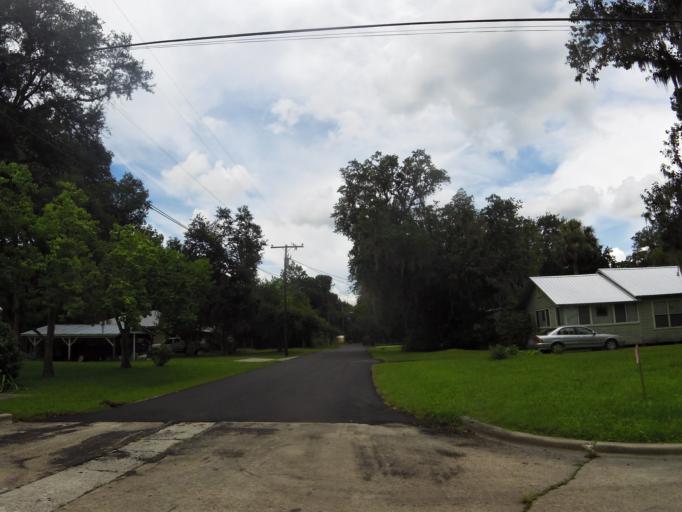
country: US
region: Florida
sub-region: Putnam County
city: East Palatka
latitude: 29.7191
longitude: -81.5048
